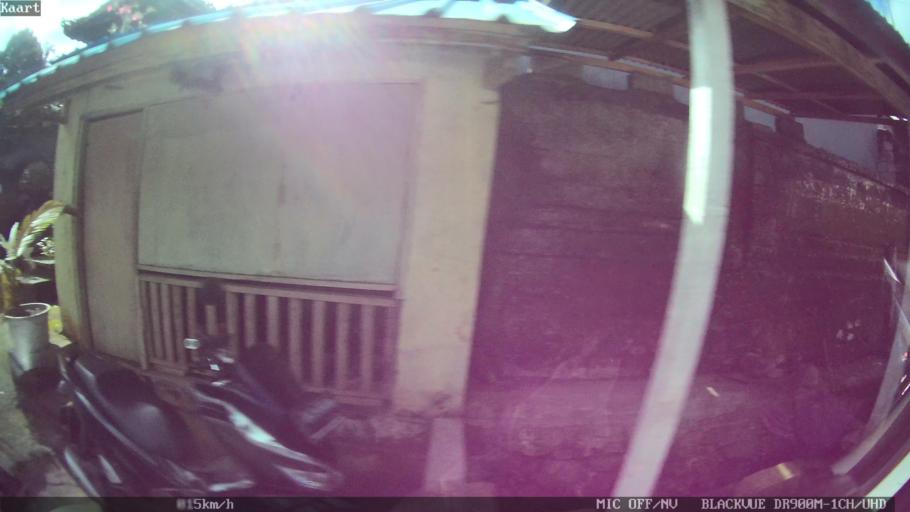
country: ID
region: Bali
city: Banjar Pesalakan
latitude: -8.5062
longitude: 115.3080
